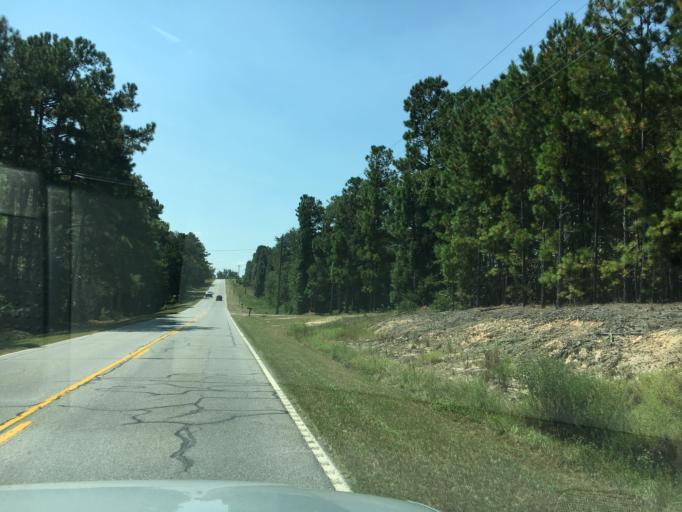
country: US
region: South Carolina
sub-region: Lexington County
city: Batesburg
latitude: 33.7983
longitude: -81.6408
